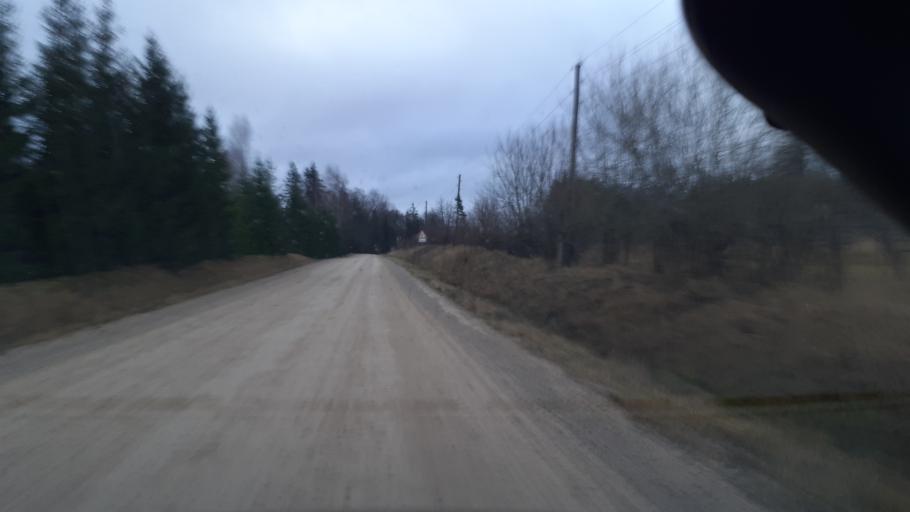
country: LV
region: Alsunga
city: Alsunga
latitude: 56.9088
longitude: 21.7241
